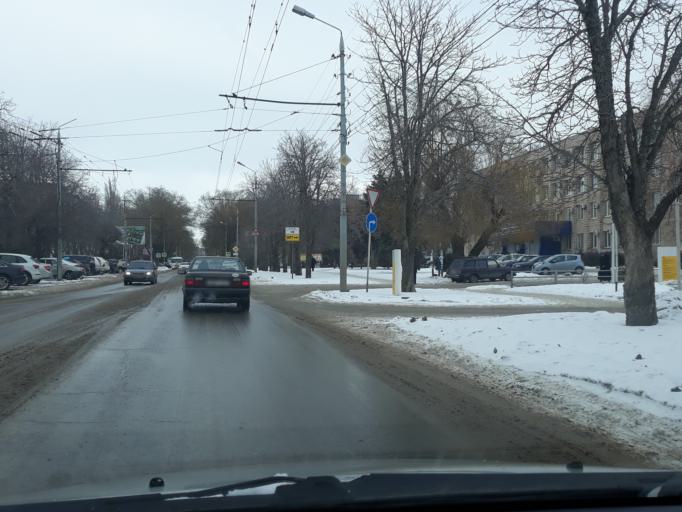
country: RU
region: Rostov
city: Taganrog
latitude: 47.2527
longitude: 38.9179
